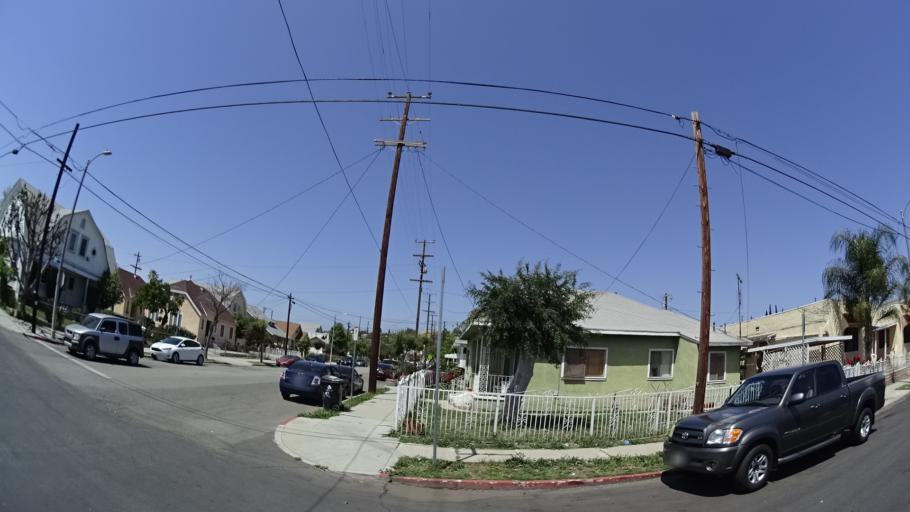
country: US
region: California
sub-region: Los Angeles County
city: Boyle Heights
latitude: 34.0702
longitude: -118.2064
